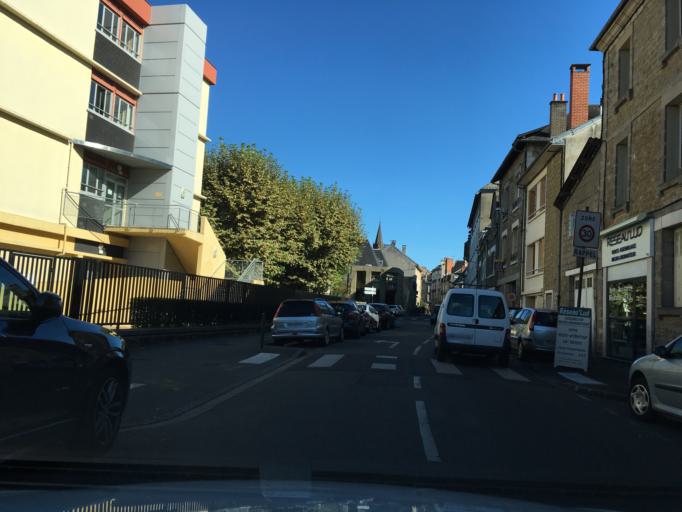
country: FR
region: Limousin
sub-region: Departement de la Correze
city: Brive-la-Gaillarde
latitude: 45.1599
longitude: 1.5289
